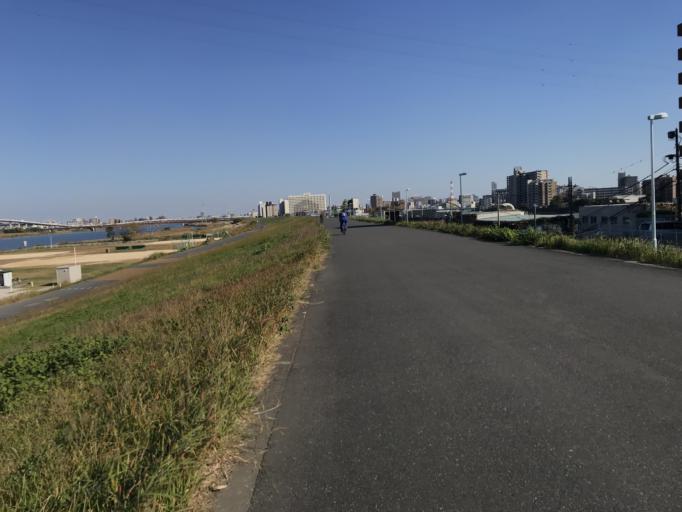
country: JP
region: Saitama
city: Soka
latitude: 35.7552
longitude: 139.7761
